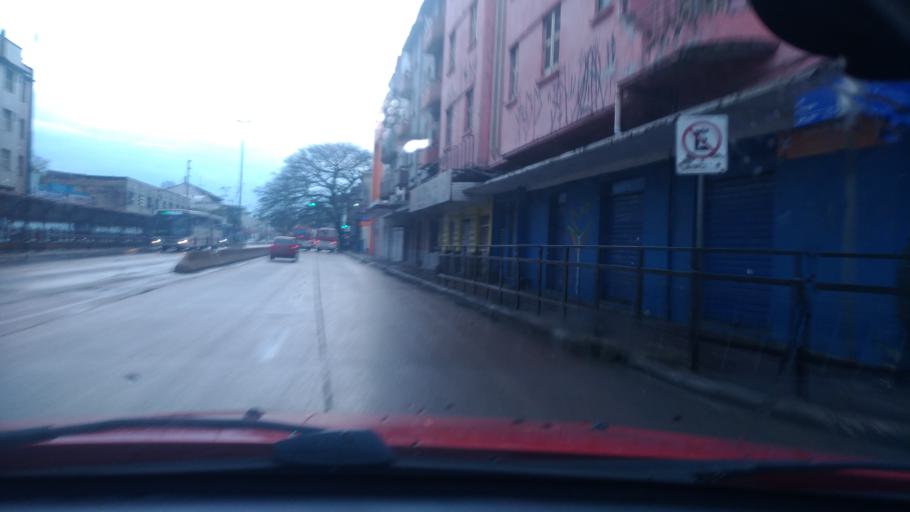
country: BR
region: Rio Grande do Sul
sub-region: Porto Alegre
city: Porto Alegre
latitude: -30.0249
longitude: -51.2148
